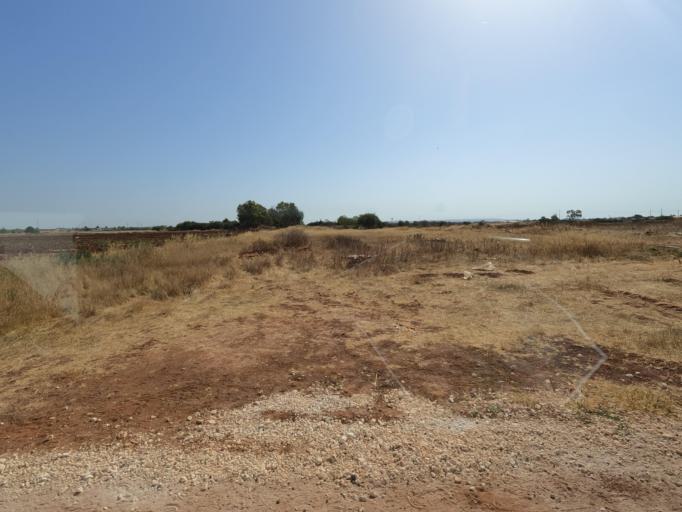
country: CY
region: Ammochostos
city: Liopetri
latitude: 34.9853
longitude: 33.8821
